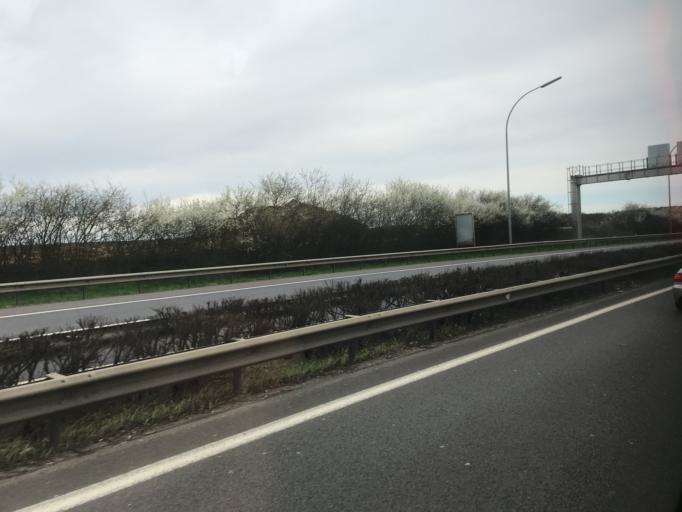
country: LU
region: Luxembourg
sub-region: Canton d'Esch-sur-Alzette
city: Leudelange
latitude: 49.5631
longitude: 6.0789
